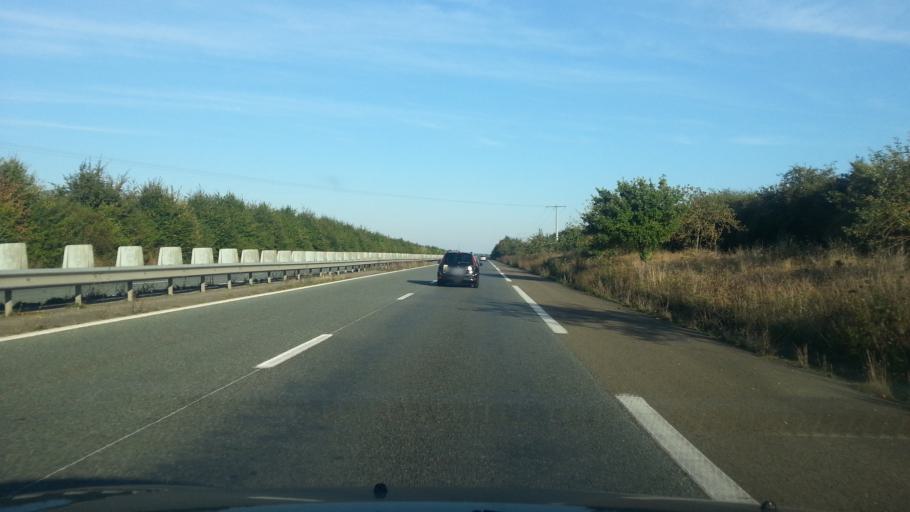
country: FR
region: Picardie
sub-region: Departement de l'Oise
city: Bresles
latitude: 49.4142
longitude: 2.2701
